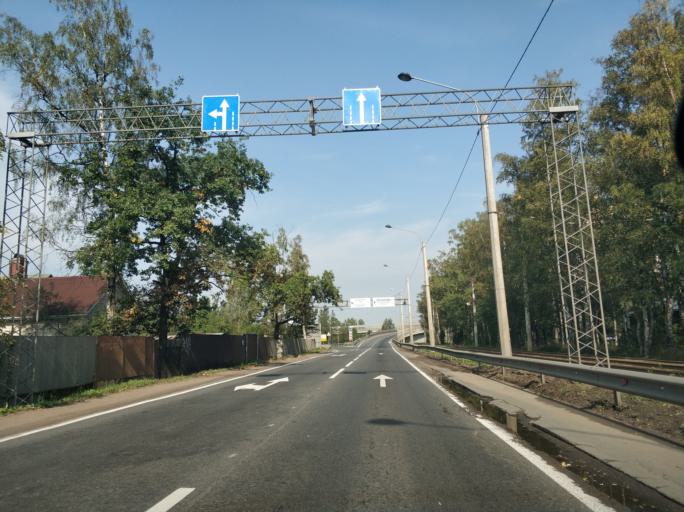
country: RU
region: St.-Petersburg
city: Krasnogvargeisky
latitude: 59.9776
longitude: 30.5059
